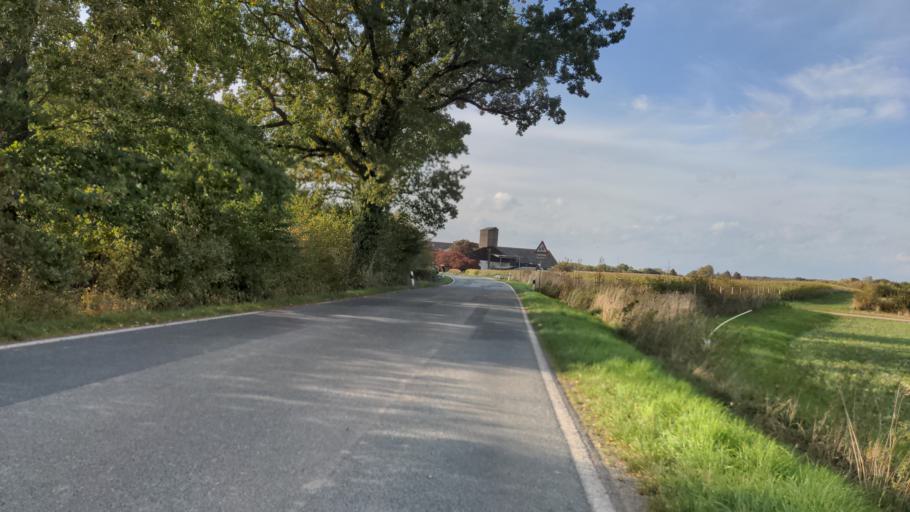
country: DE
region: Schleswig-Holstein
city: Monkhagen
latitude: 53.9538
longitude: 10.5396
